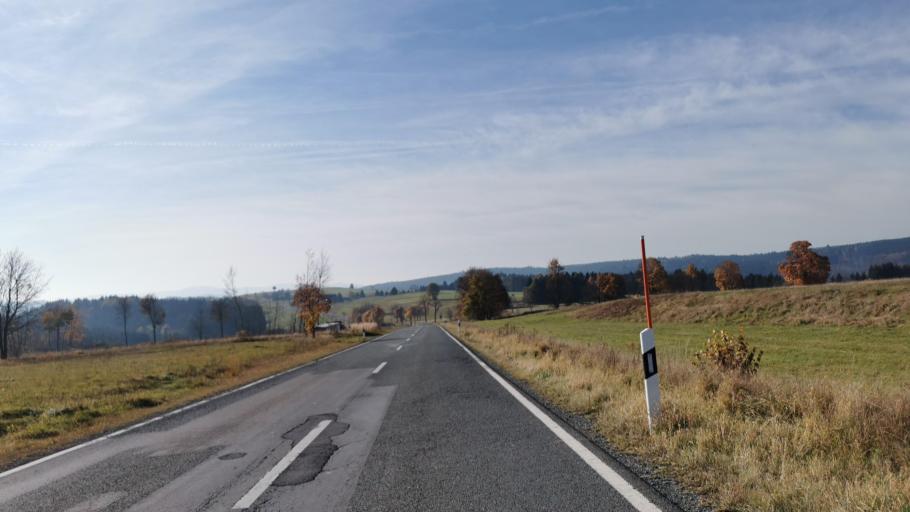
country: DE
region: Bavaria
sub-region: Upper Franconia
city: Nordhalben
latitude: 50.3662
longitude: 11.5041
